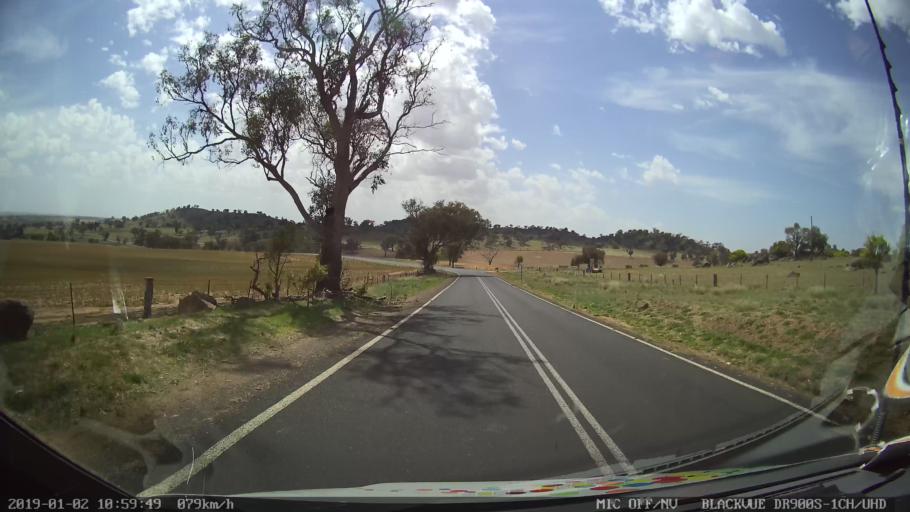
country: AU
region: New South Wales
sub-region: Cootamundra
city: Cootamundra
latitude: -34.6118
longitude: 148.3103
